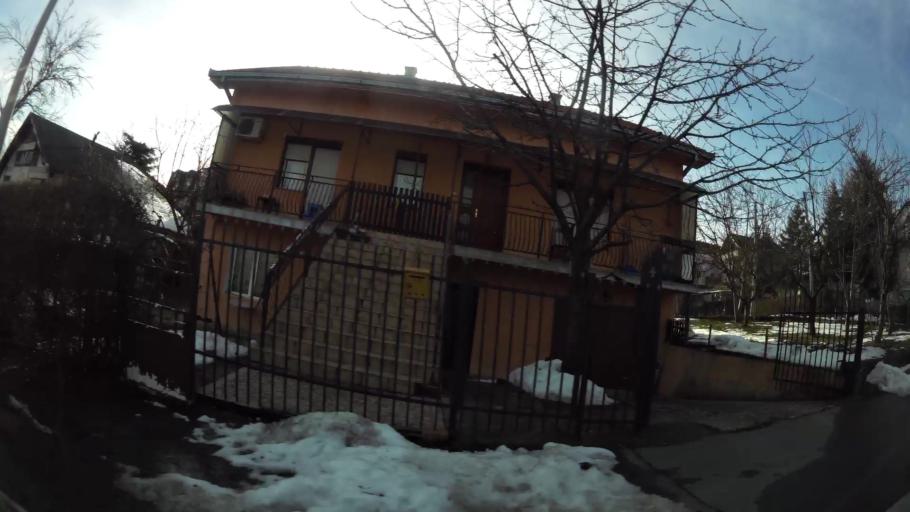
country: RS
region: Central Serbia
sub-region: Belgrade
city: Rakovica
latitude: 44.7250
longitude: 20.4325
